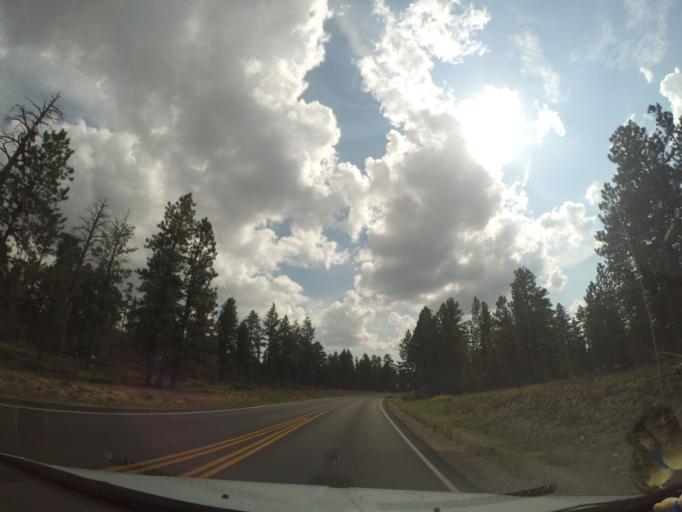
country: US
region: Utah
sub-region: Garfield County
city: Panguitch
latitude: 37.6237
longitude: -112.1713
